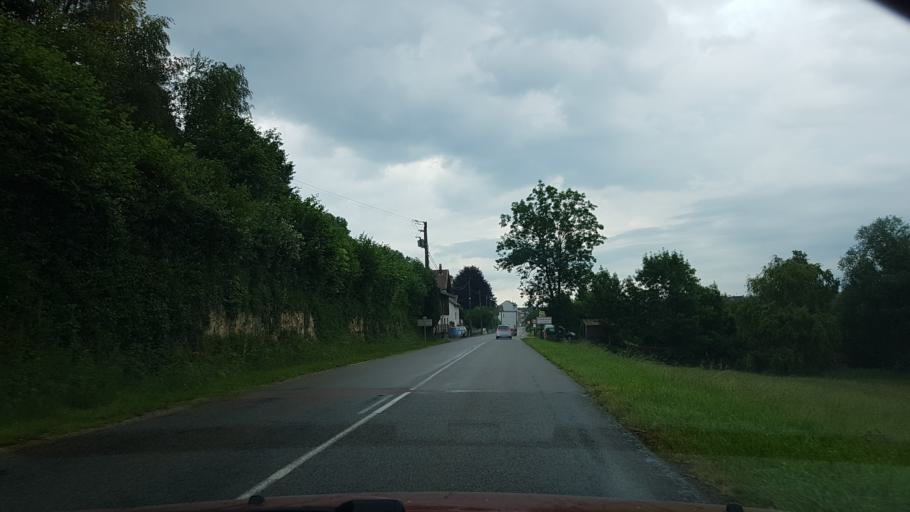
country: FR
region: Franche-Comte
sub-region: Departement du Jura
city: Clairvaux-les-Lacs
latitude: 46.5685
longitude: 5.7448
